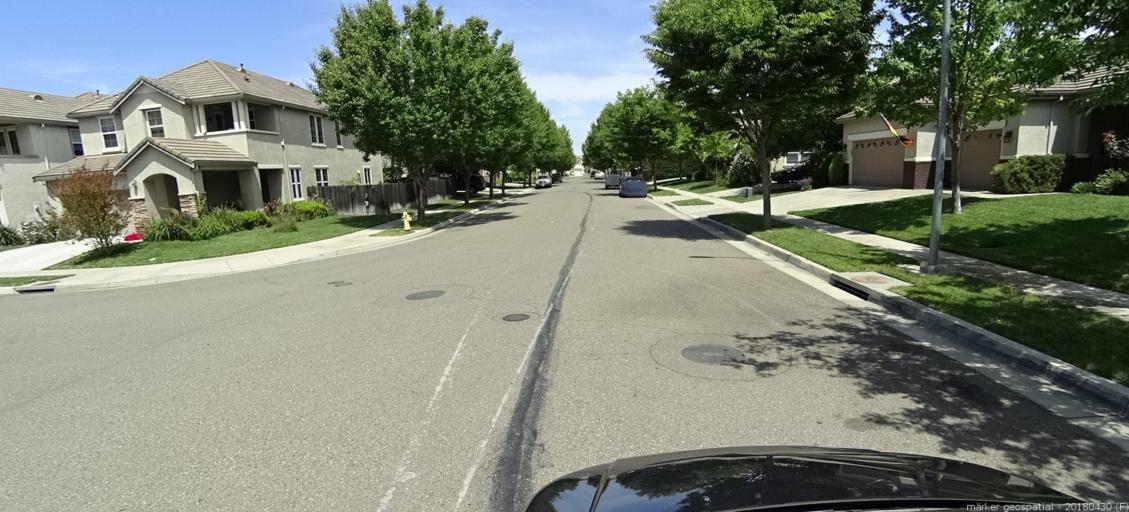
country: US
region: California
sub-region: Yolo County
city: West Sacramento
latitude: 38.5471
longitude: -121.5318
